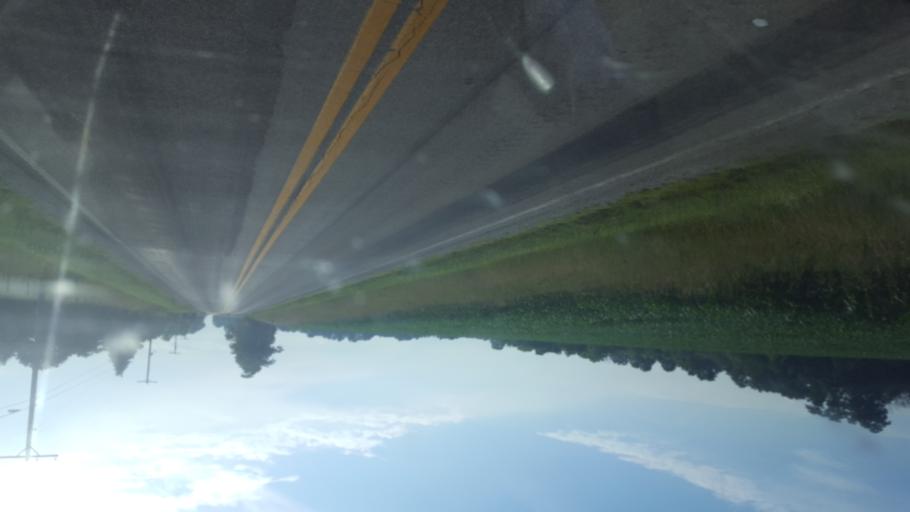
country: US
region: Ohio
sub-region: Ashland County
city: Ashland
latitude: 40.7729
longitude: -82.3017
